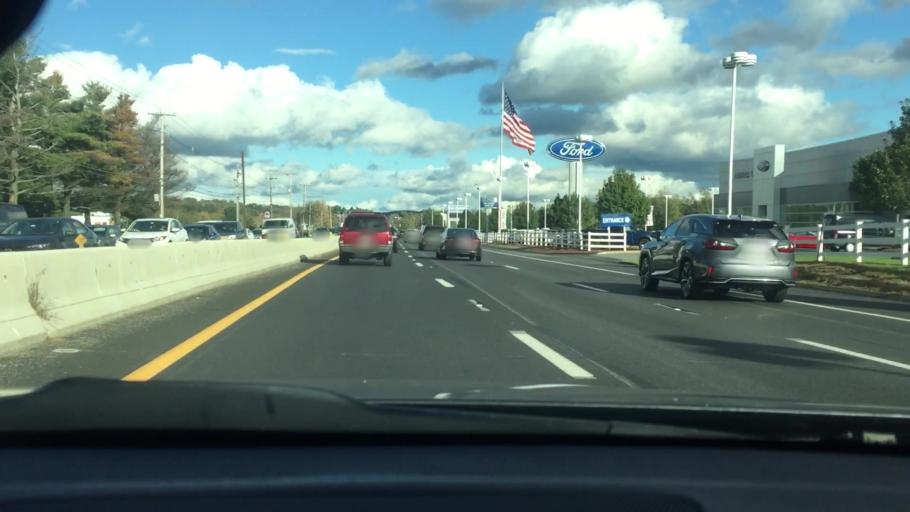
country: US
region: Massachusetts
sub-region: Worcester County
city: Westborough
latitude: 42.2827
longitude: -71.6522
